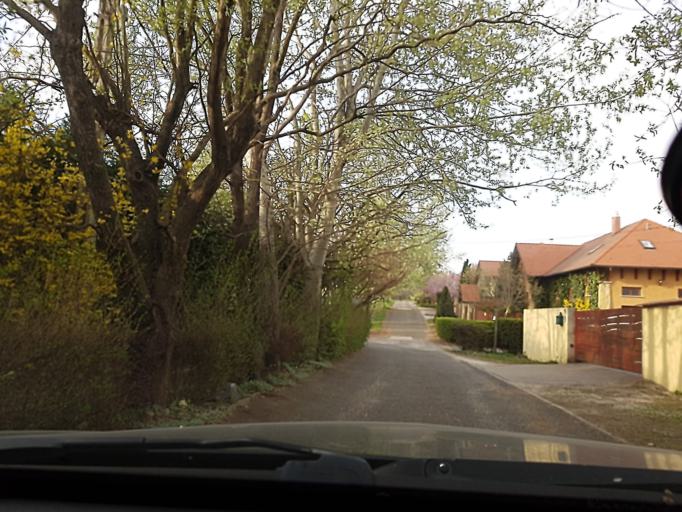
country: HU
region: Pest
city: Piliscsaba
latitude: 47.6269
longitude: 18.8408
